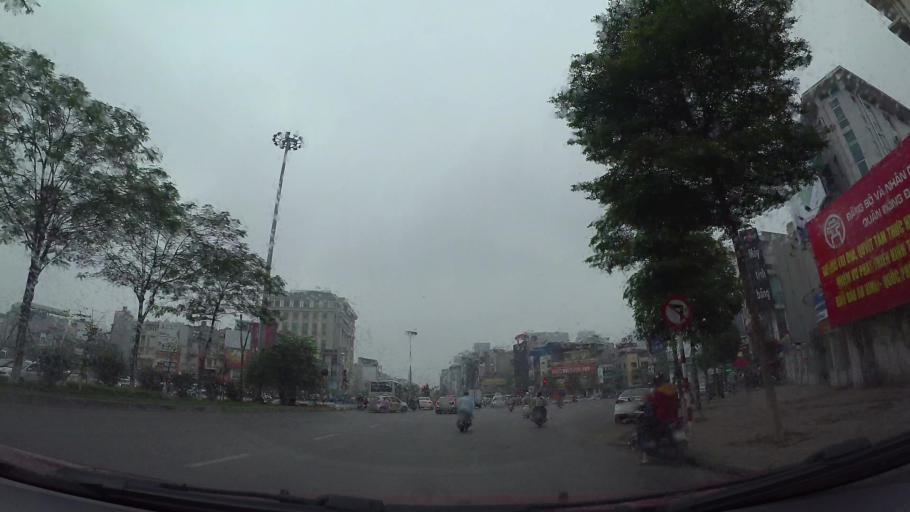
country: VN
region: Ha Noi
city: Dong Da
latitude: 21.0187
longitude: 105.8291
